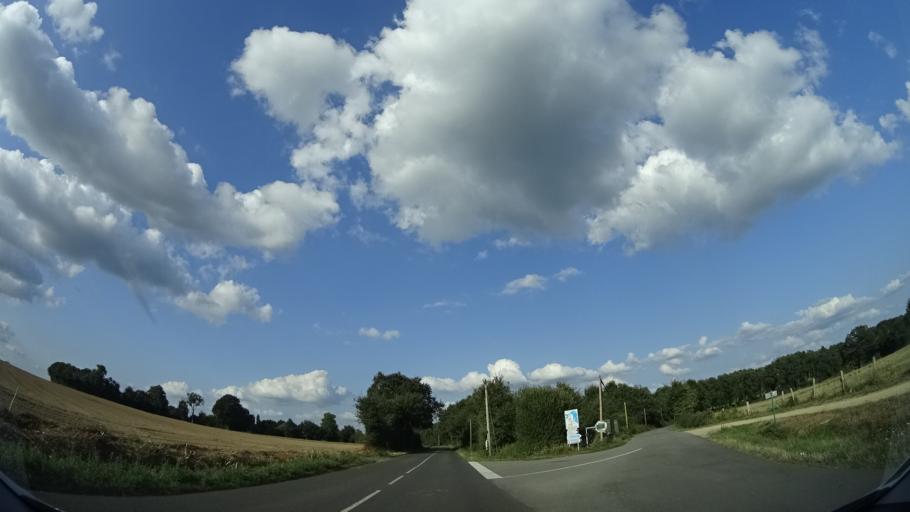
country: FR
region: Pays de la Loire
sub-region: Departement de la Loire-Atlantique
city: Suce-sur-Erdre
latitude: 47.3661
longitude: -1.5252
